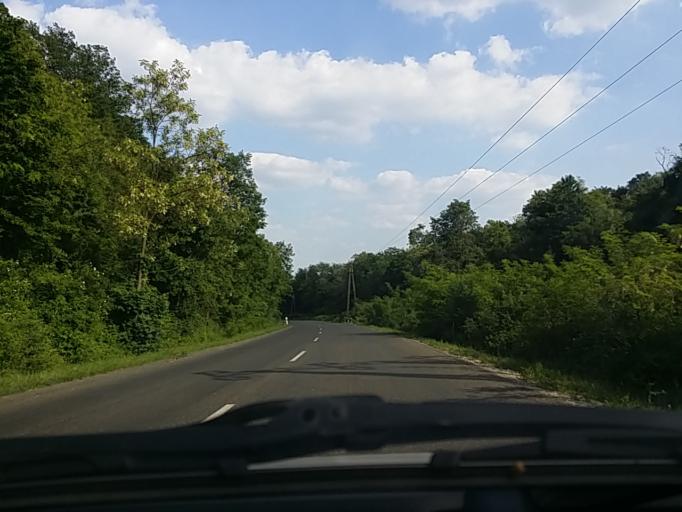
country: HU
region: Pest
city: Pilisszentkereszt
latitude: 47.6879
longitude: 18.9143
